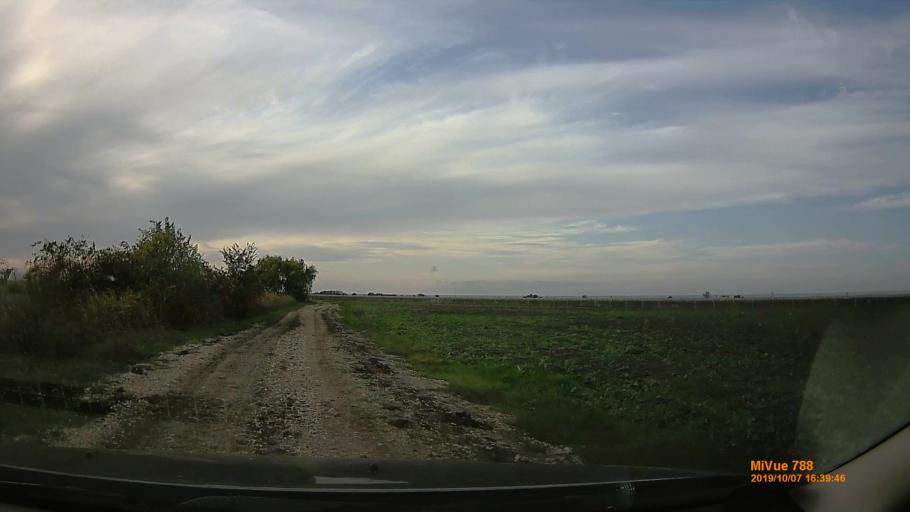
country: HU
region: Bekes
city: Szarvas
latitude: 46.8179
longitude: 20.6006
